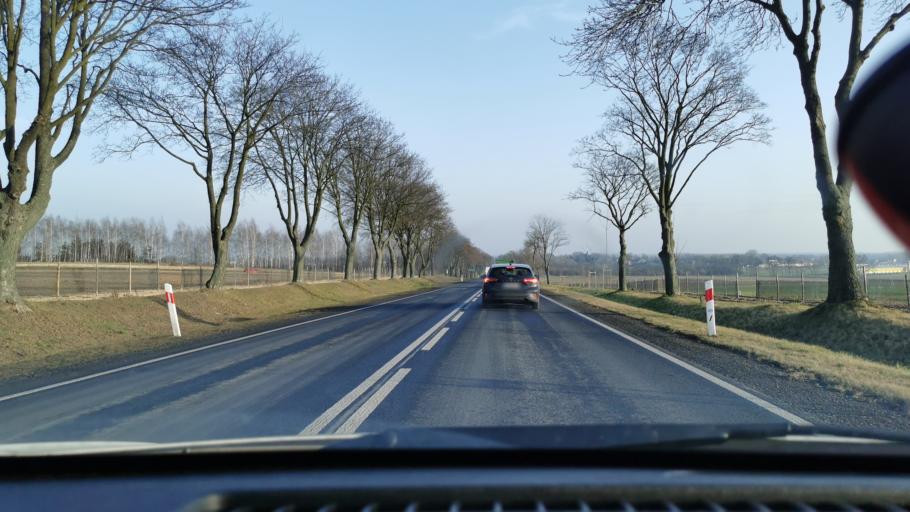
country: PL
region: Lodz Voivodeship
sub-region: Powiat sieradzki
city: Wroblew
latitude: 51.6166
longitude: 18.5992
